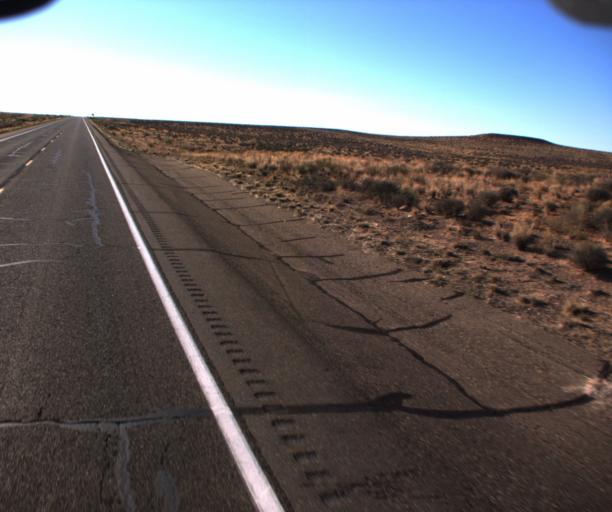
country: US
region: Arizona
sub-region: Coconino County
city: Page
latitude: 36.9709
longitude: -111.5150
